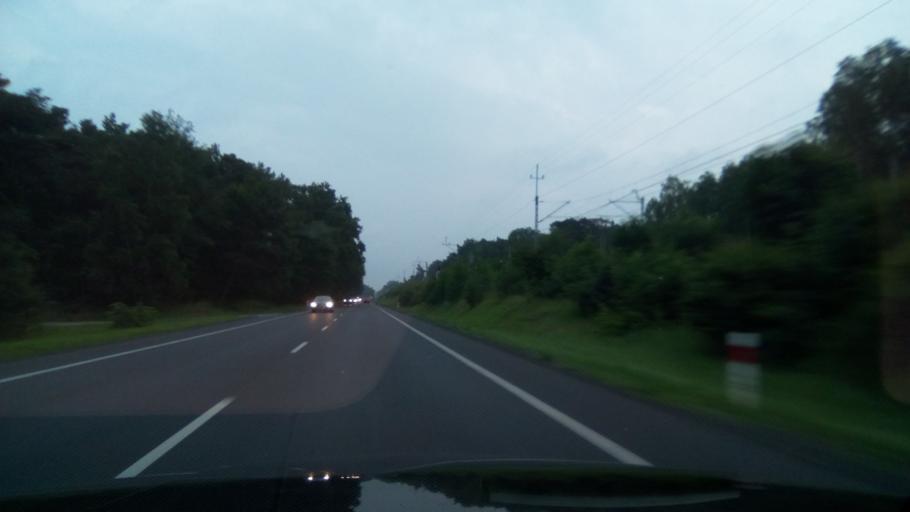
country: PL
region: Greater Poland Voivodeship
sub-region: Powiat poznanski
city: Kostrzyn
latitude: 52.4704
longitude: 17.2005
